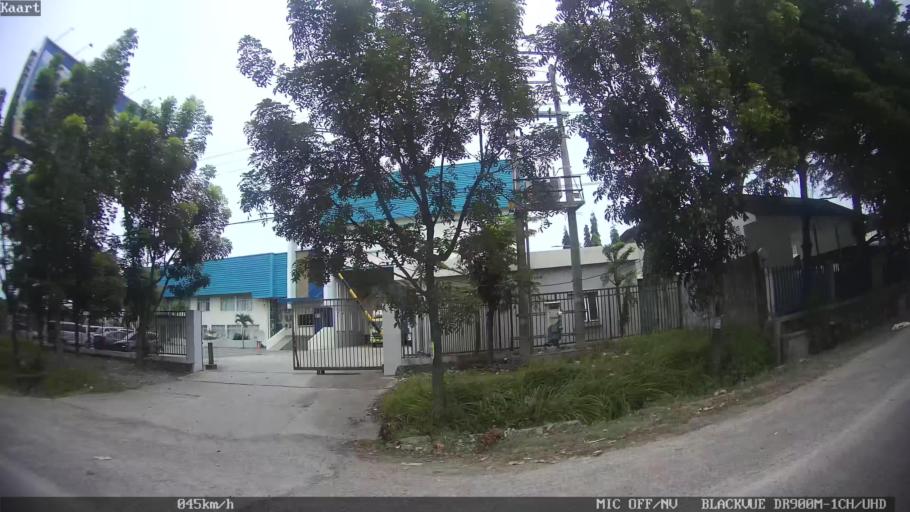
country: ID
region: Lampung
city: Bandarlampung
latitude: -5.4161
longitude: 105.2957
